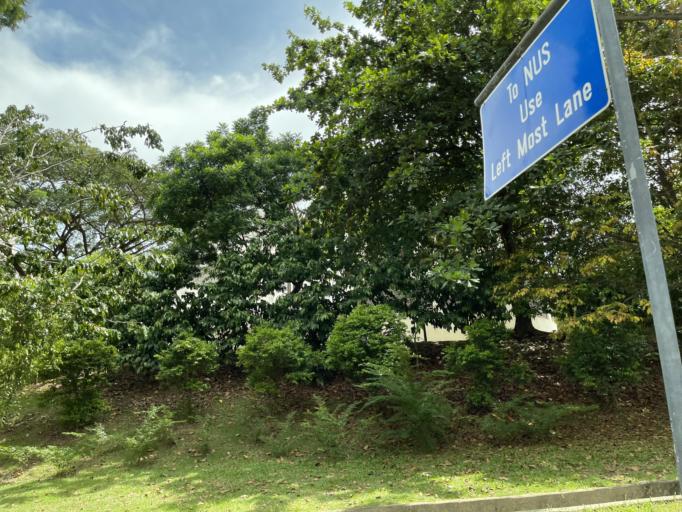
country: SG
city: Singapore
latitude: 1.3026
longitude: 103.7716
